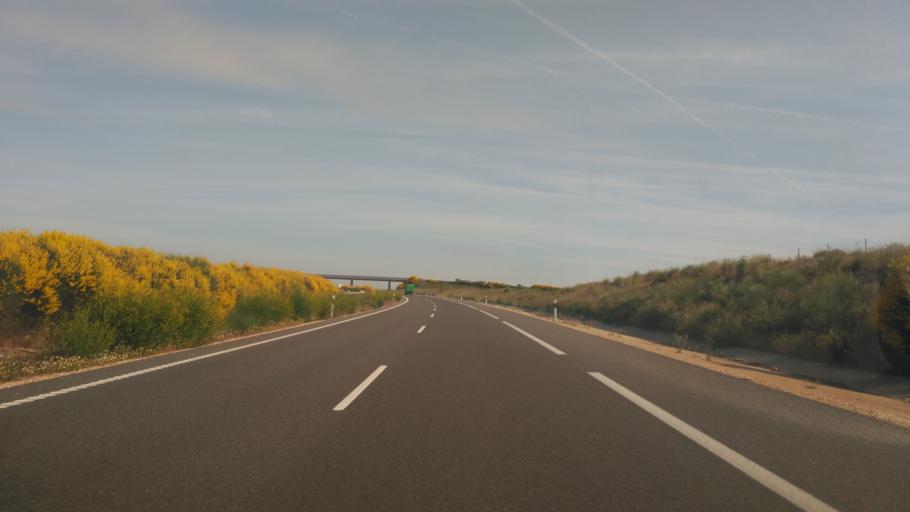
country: ES
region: Castille and Leon
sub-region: Provincia de Salamanca
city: Castellanos de Villiquera
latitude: 41.0472
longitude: -5.6680
